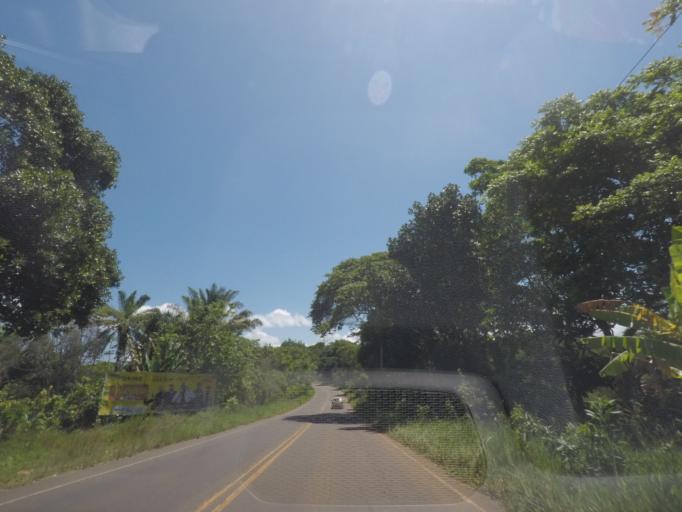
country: BR
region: Bahia
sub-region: Valenca
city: Valenca
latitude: -13.3397
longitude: -39.0648
